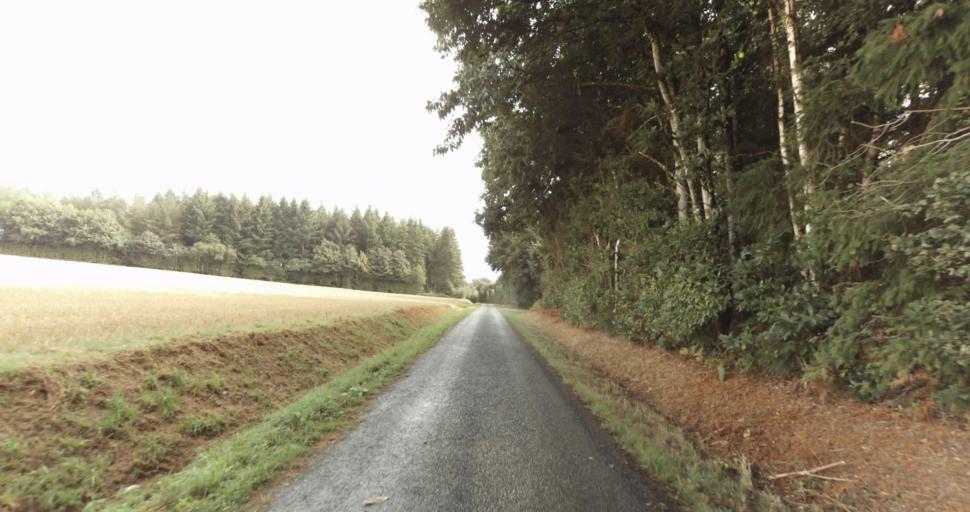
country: FR
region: Lower Normandy
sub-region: Departement de l'Orne
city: Sainte-Gauburge-Sainte-Colombe
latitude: 48.6766
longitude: 0.3812
